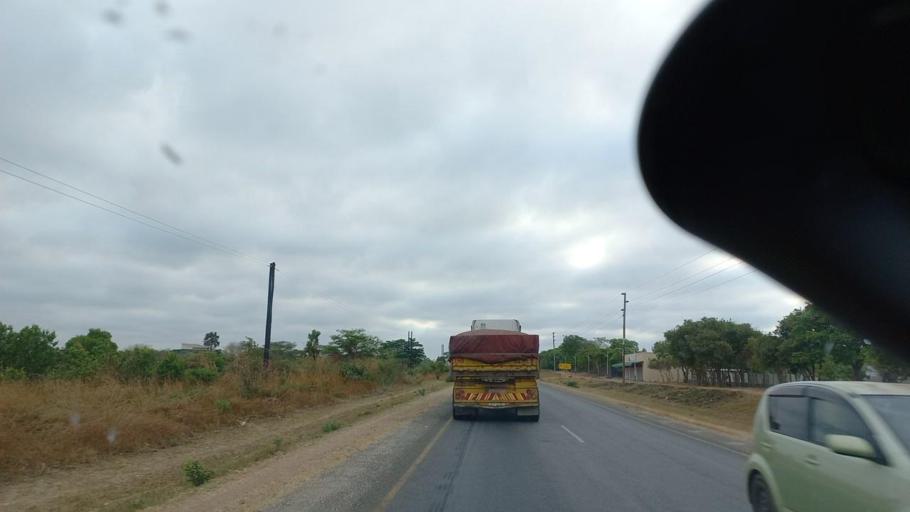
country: ZM
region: Lusaka
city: Chongwe
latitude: -15.3516
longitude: 28.5565
